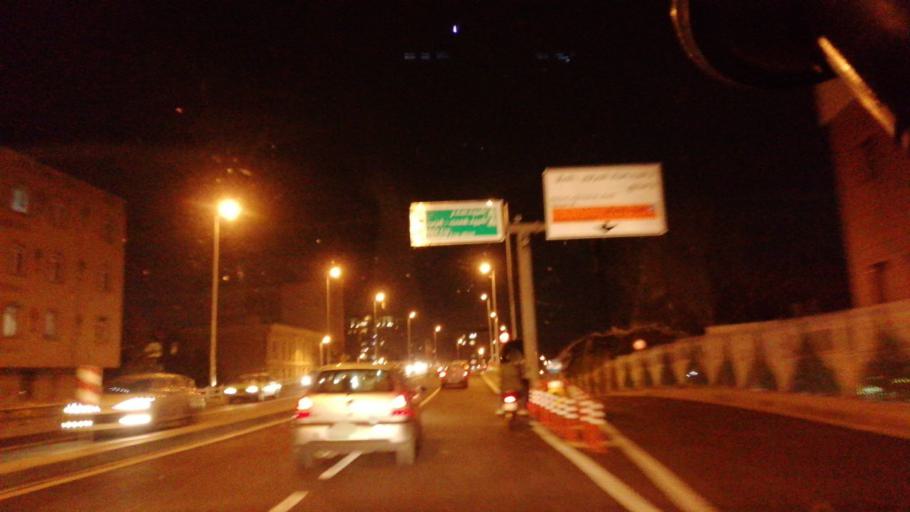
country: IR
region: Tehran
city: Tajrish
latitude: 35.7928
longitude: 51.4880
